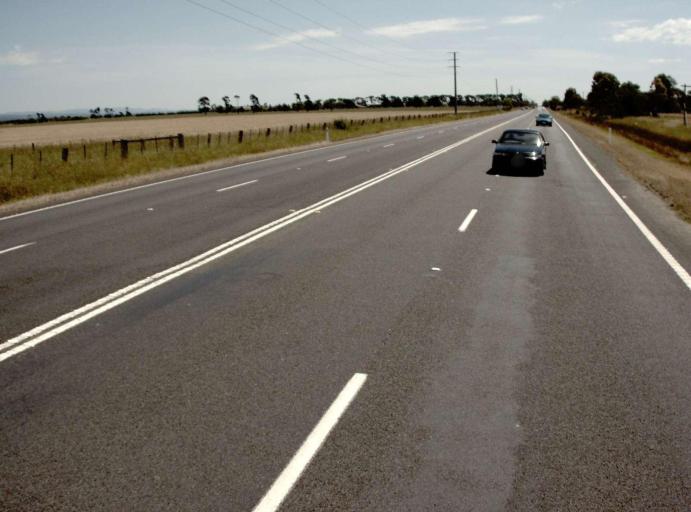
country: AU
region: Victoria
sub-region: Wellington
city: Sale
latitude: -38.1029
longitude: 146.9359
